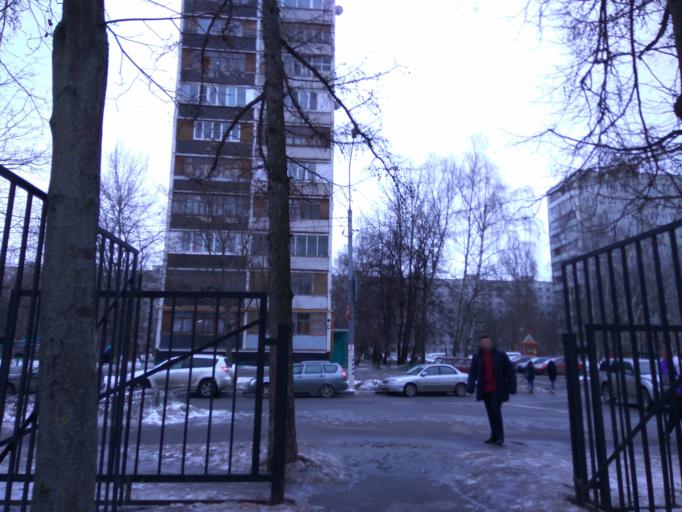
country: RU
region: Moscow
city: Biryulevo
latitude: 55.5960
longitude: 37.6655
